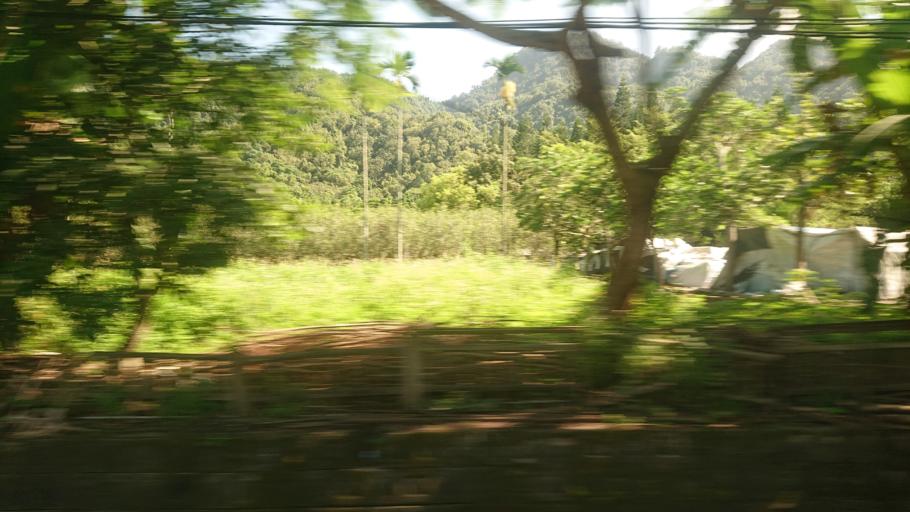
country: TW
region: Taiwan
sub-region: Nantou
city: Puli
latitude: 24.0612
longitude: 120.8952
